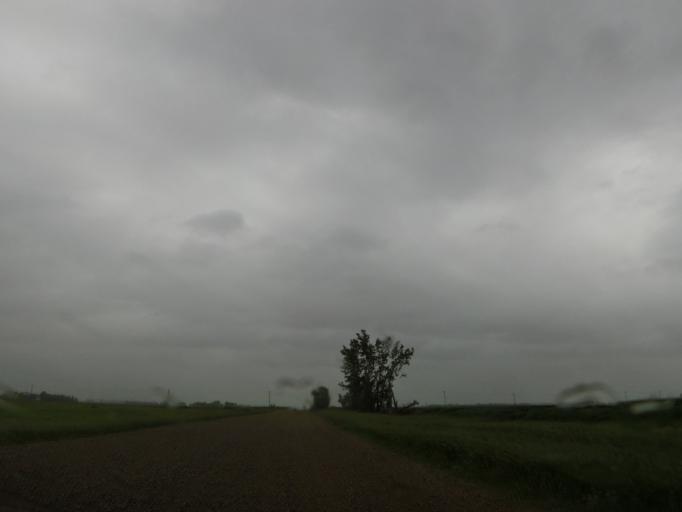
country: US
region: North Dakota
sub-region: Walsh County
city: Grafton
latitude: 48.4383
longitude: -97.4053
